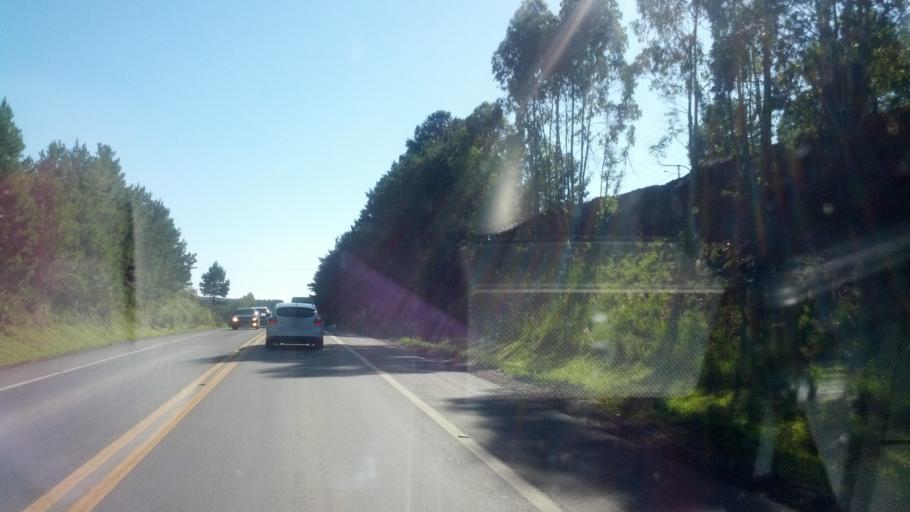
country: BR
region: Santa Catarina
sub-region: Lages
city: Lages
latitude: -27.7839
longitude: -50.2570
